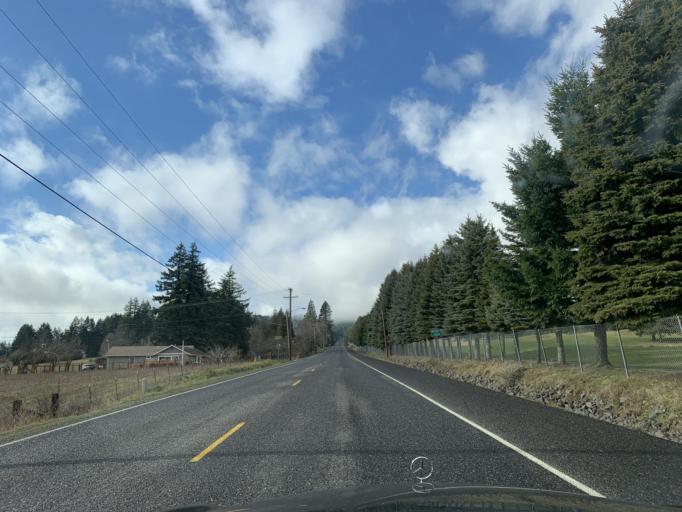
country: US
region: Washington
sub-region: Skamania County
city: Carson
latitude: 45.7261
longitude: -121.8038
